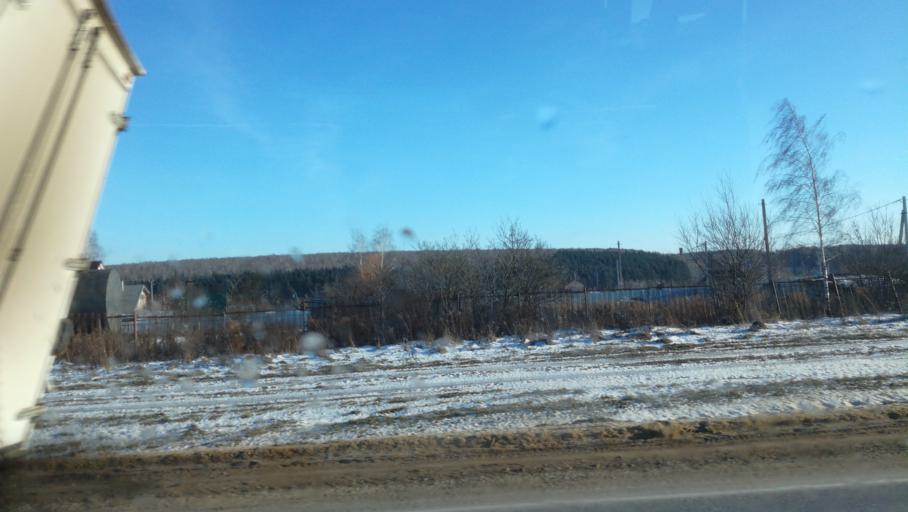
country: RU
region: Tula
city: Barsuki
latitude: 54.1702
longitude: 37.4583
